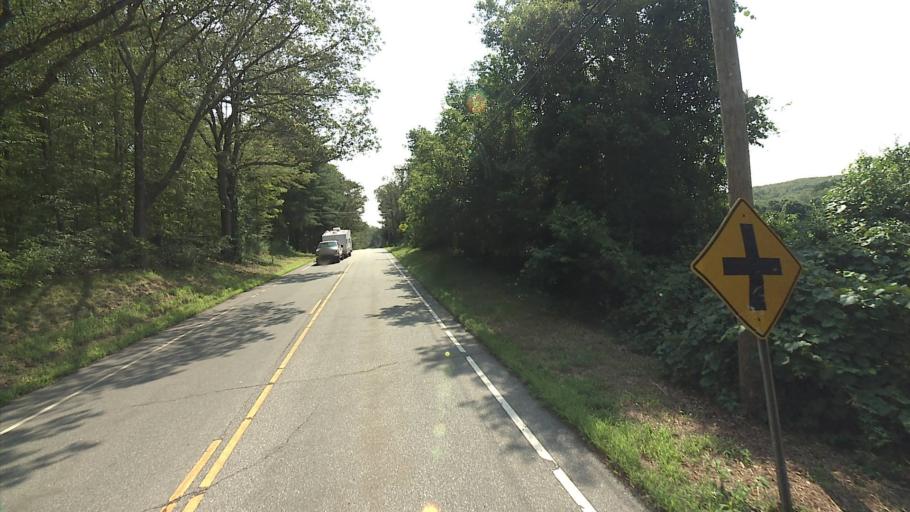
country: US
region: Connecticut
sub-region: New London County
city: Colchester
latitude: 41.5718
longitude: -72.2354
